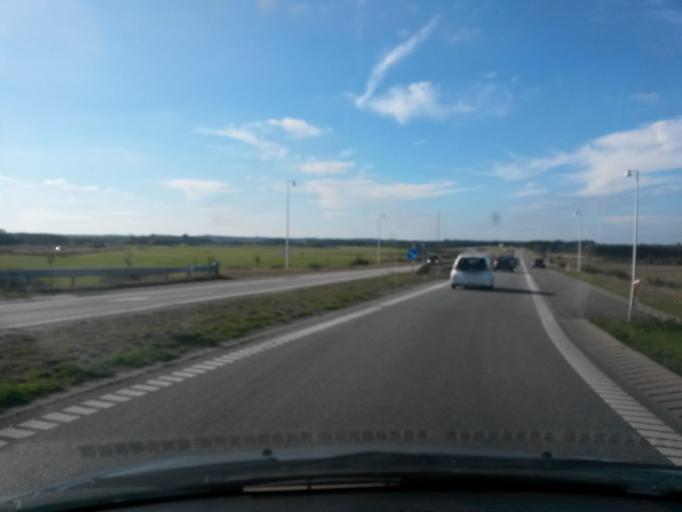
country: DK
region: Central Jutland
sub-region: Silkeborg Kommune
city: Silkeborg
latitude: 56.1467
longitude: 9.4542
